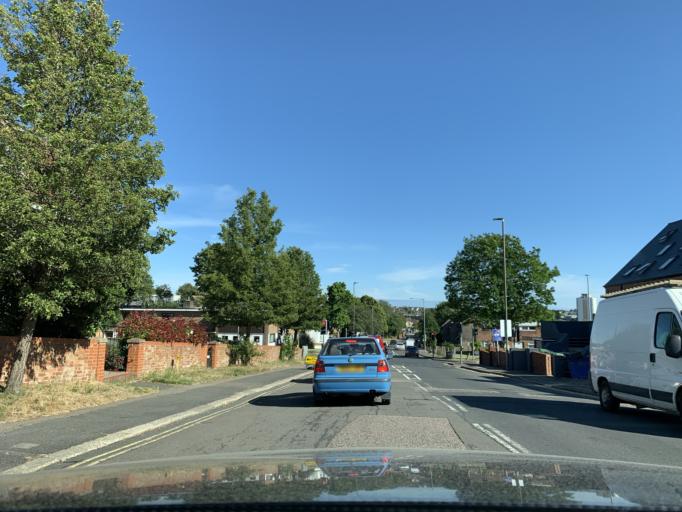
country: GB
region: England
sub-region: East Sussex
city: Saint Leonards-on-Sea
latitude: 50.8786
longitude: 0.5496
